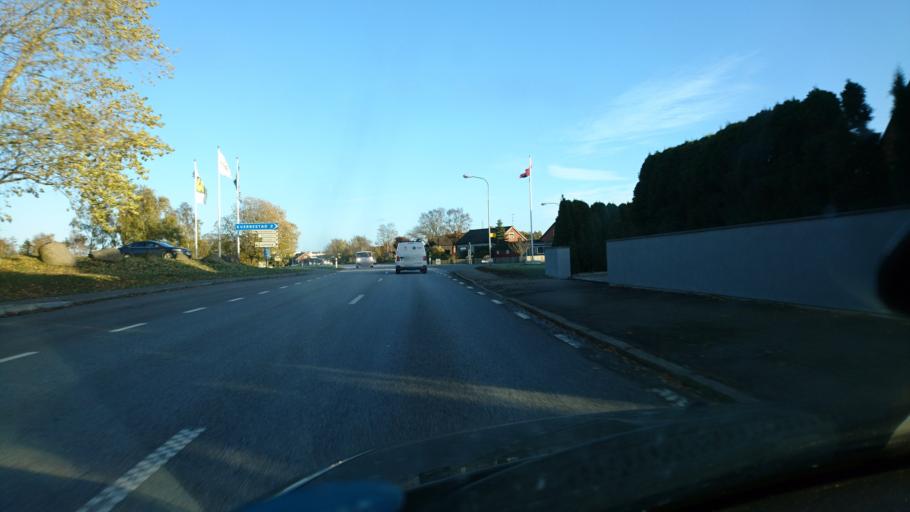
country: SE
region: Skane
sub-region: Tomelilla Kommun
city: Tomelilla
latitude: 55.5436
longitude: 14.0406
